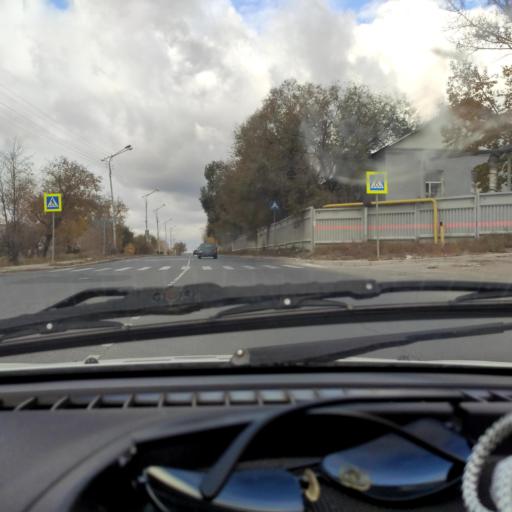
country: RU
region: Samara
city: Zhigulevsk
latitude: 53.4733
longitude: 49.5383
